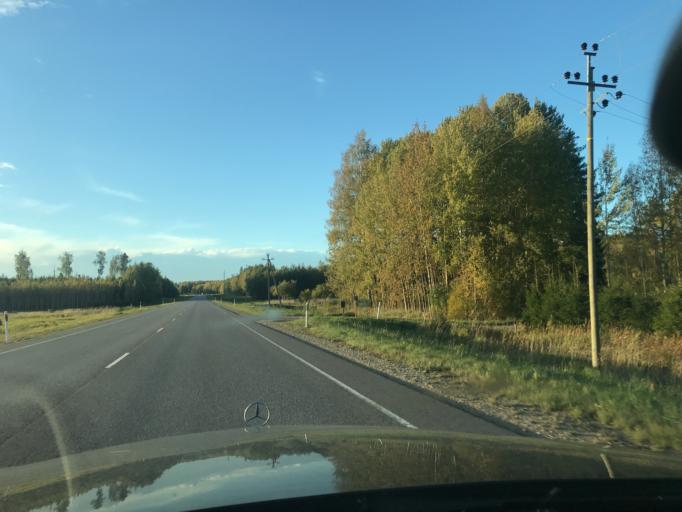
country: EE
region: Vorumaa
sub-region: Voru linn
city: Voru
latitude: 57.8431
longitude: 27.0491
